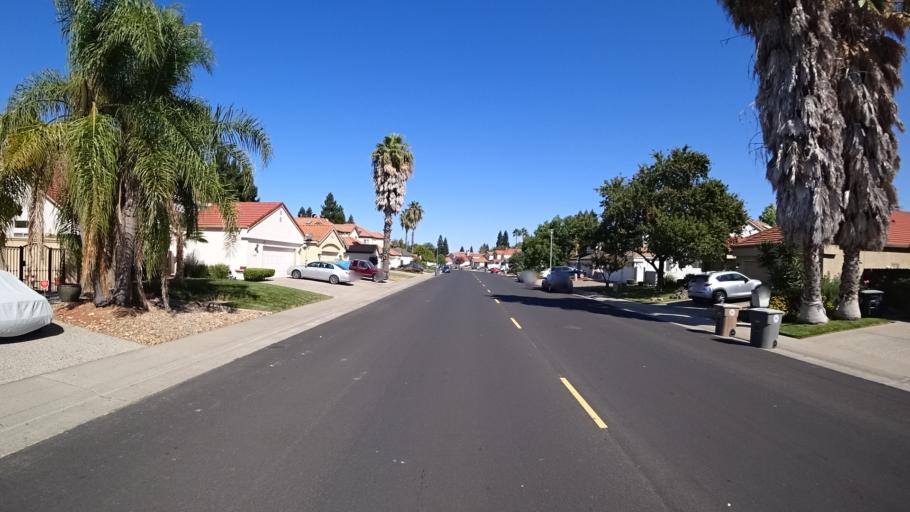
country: US
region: California
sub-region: Sacramento County
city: Laguna
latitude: 38.4282
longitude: -121.4321
